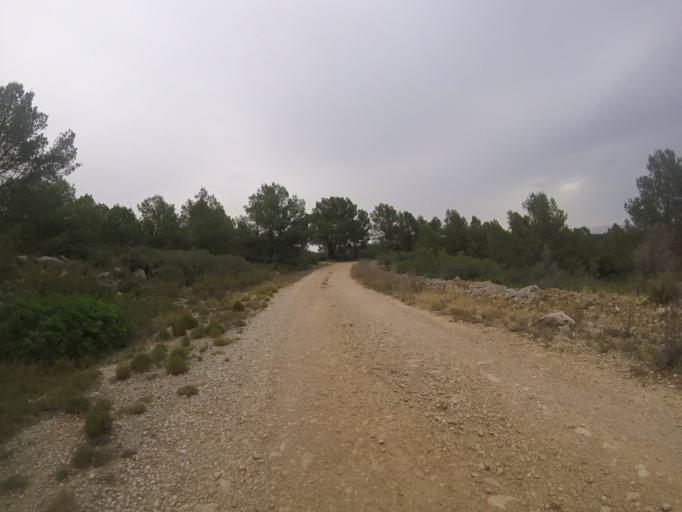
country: ES
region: Valencia
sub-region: Provincia de Castello
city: Alcoceber
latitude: 40.2818
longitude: 0.2832
